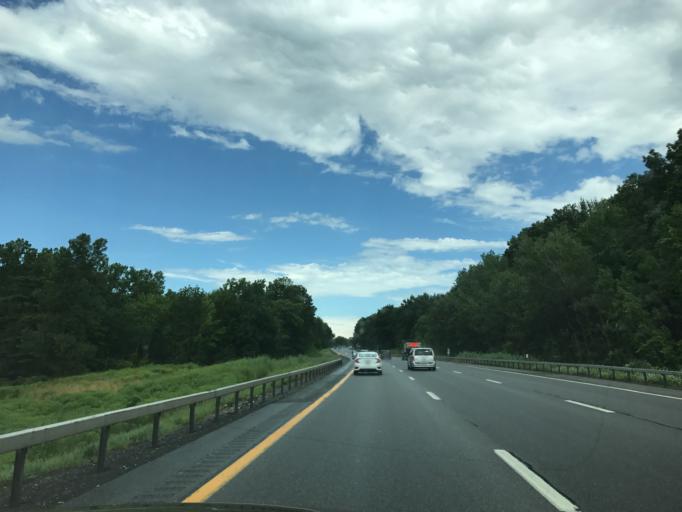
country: US
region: New York
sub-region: Albany County
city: Cohoes
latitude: 42.8062
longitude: -73.7650
